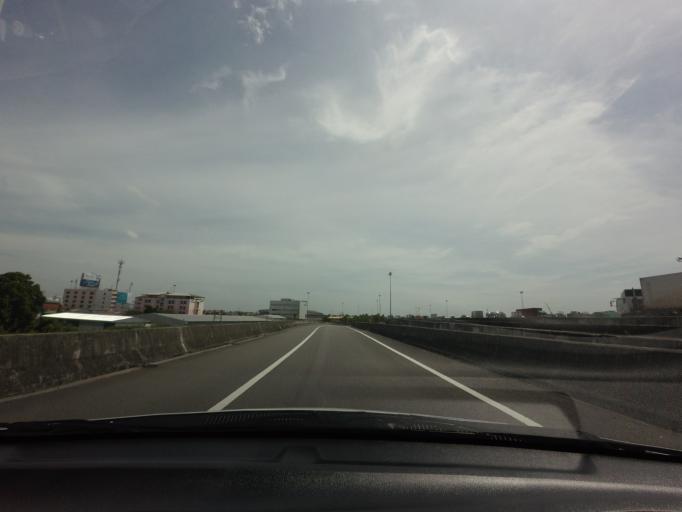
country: TH
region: Bangkok
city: Bang Na
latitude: 13.6162
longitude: 100.6614
